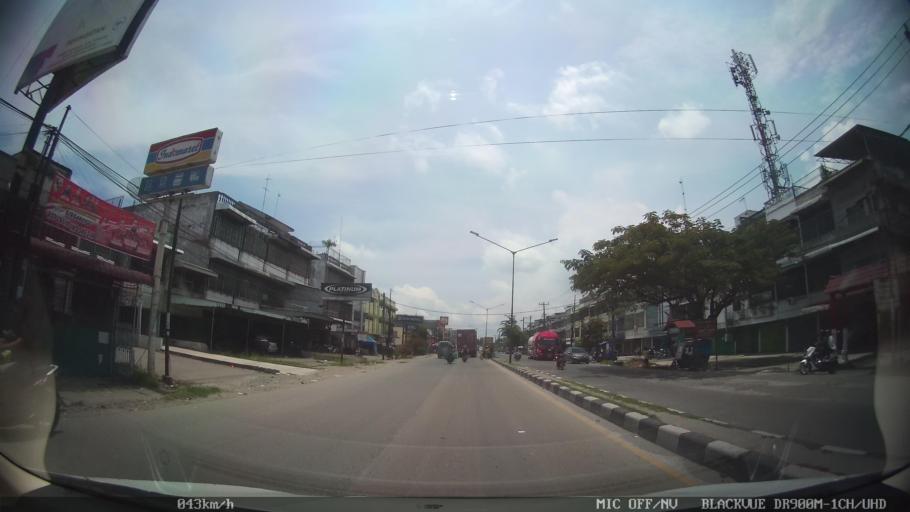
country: ID
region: North Sumatra
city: Labuhan Deli
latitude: 3.7224
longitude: 98.6795
